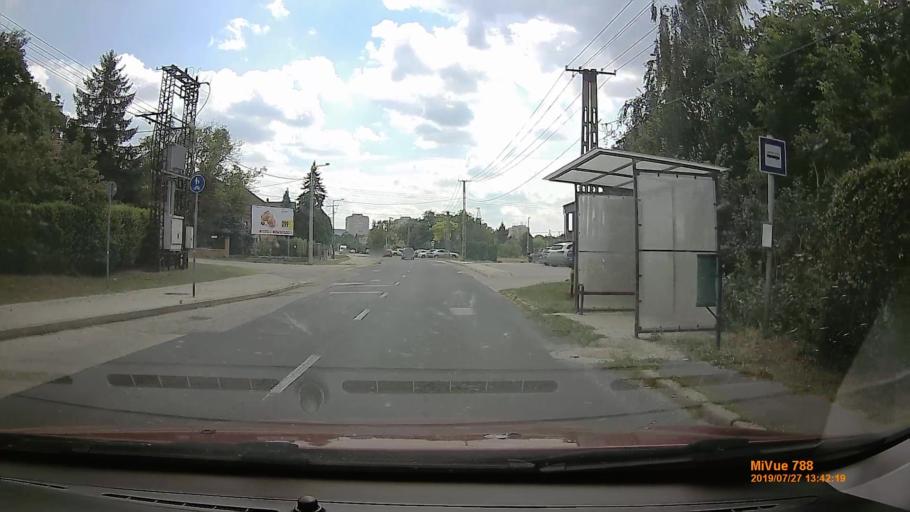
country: HU
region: Veszprem
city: Ajka
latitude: 47.1152
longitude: 17.5634
